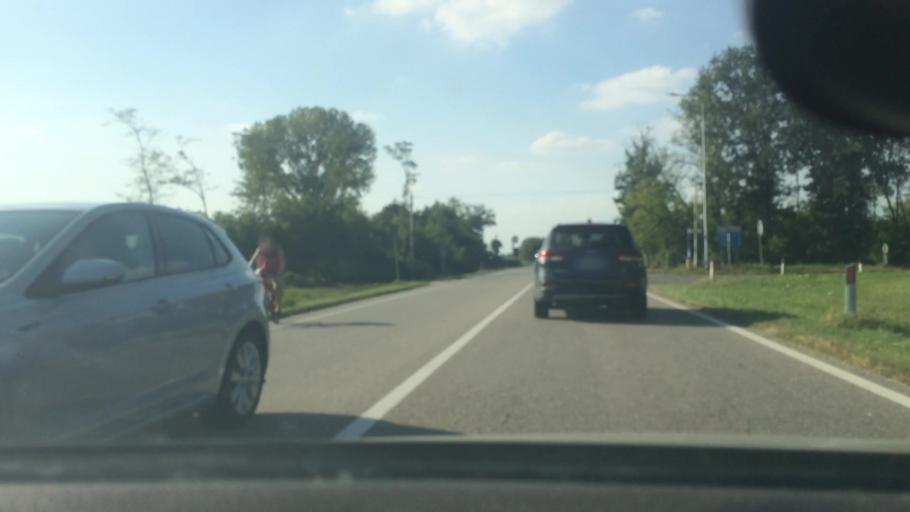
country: IT
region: Lombardy
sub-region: Citta metropolitana di Milano
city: Arconate
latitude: 45.5312
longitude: 8.8334
